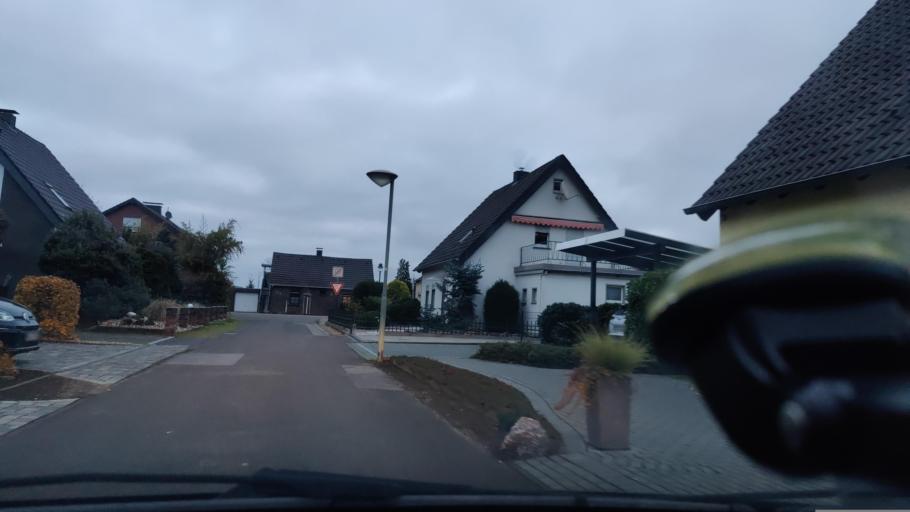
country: DE
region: North Rhine-Westphalia
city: Rheinberg
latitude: 51.5319
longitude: 6.6414
